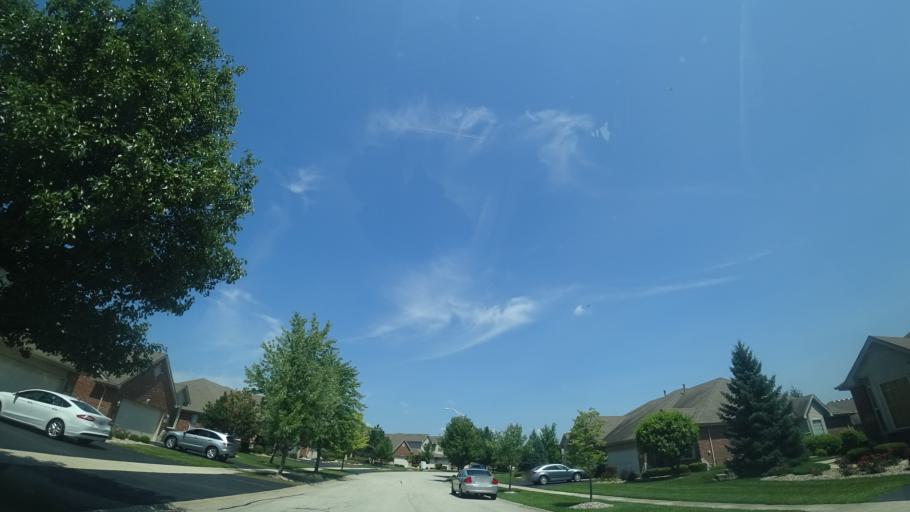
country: US
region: Illinois
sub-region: Will County
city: Mokena
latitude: 41.5610
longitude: -87.9039
